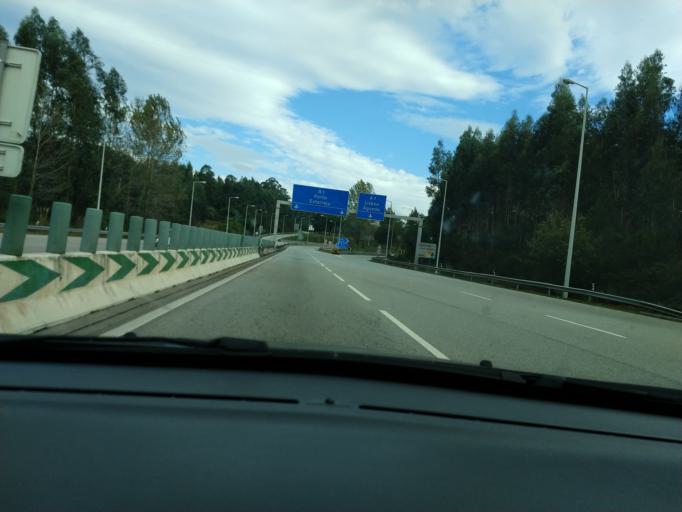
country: PT
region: Aveiro
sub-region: Albergaria-A-Velha
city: Albergaria-a-Velha
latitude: 40.6901
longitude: -8.5243
